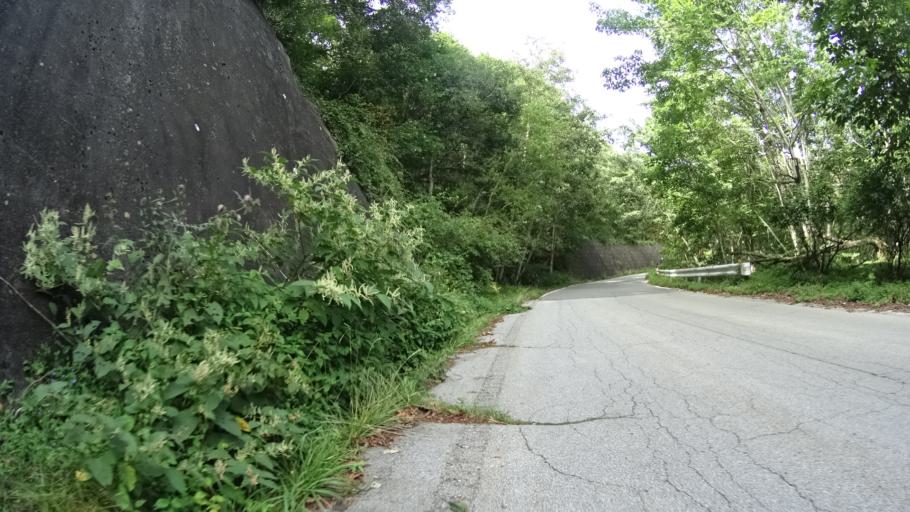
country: JP
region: Yamanashi
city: Nirasaki
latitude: 35.9136
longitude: 138.5419
